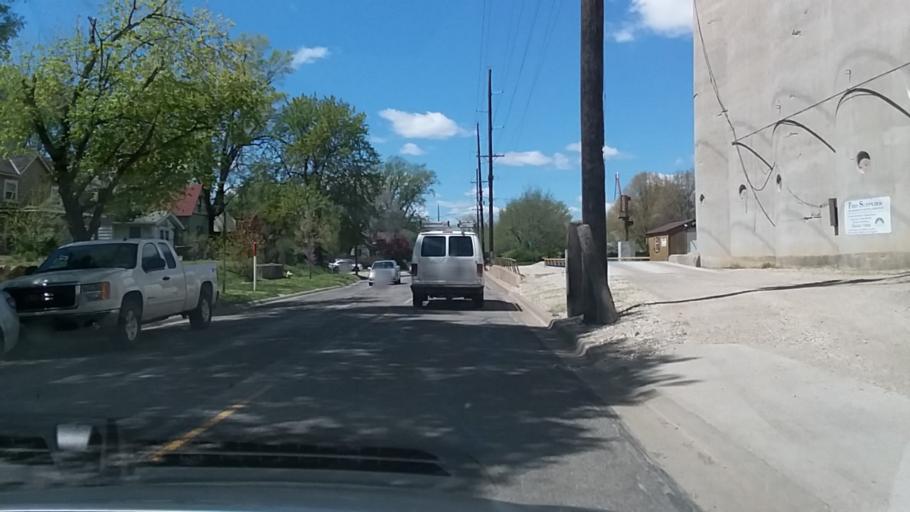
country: US
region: Kansas
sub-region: Douglas County
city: Lawrence
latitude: 38.9778
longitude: -95.2321
